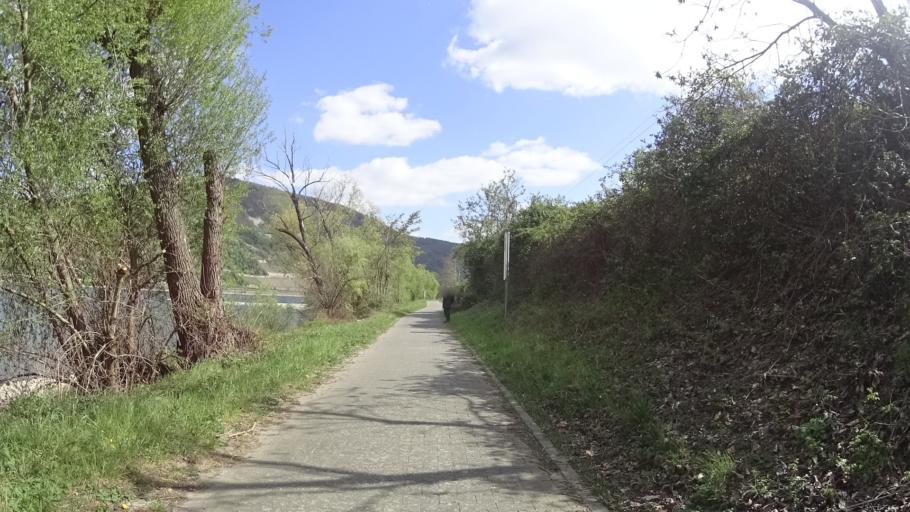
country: DE
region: Rheinland-Pfalz
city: Trechtingshausen
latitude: 50.0160
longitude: 7.8402
